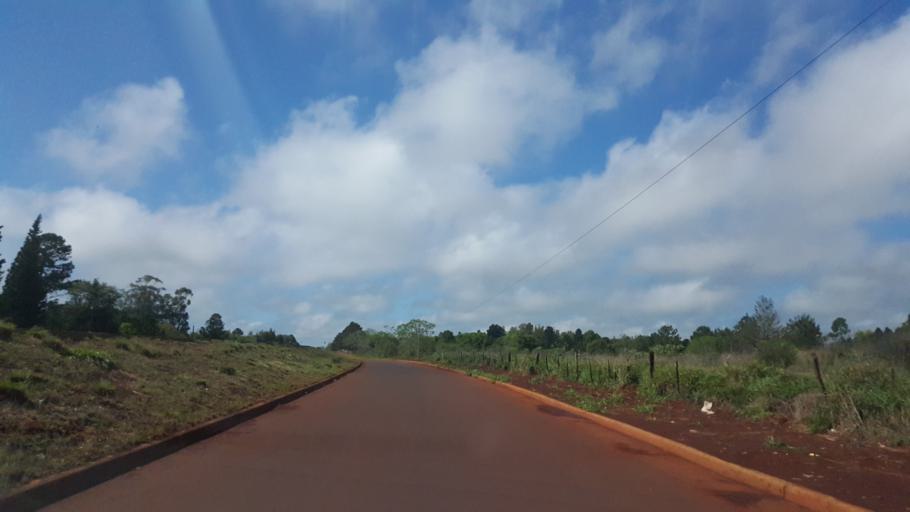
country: AR
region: Misiones
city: Garupa
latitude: -27.4909
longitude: -55.8647
